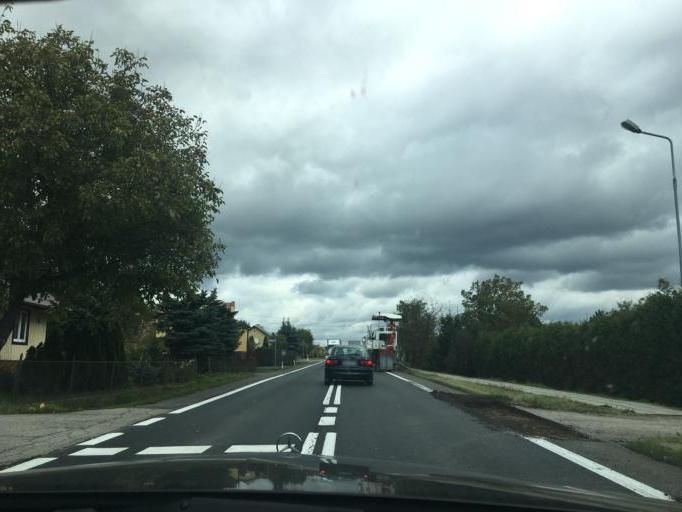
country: PL
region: Subcarpathian Voivodeship
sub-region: Powiat krosnienski
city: Miejsce Piastowe
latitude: 49.6235
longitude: 21.7667
